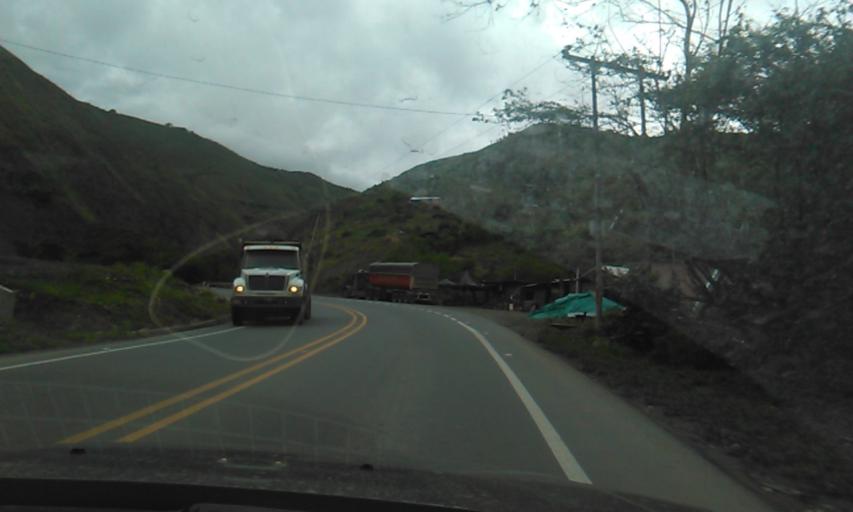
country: CO
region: Valle del Cauca
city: Dagua
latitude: 3.7778
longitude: -76.6466
